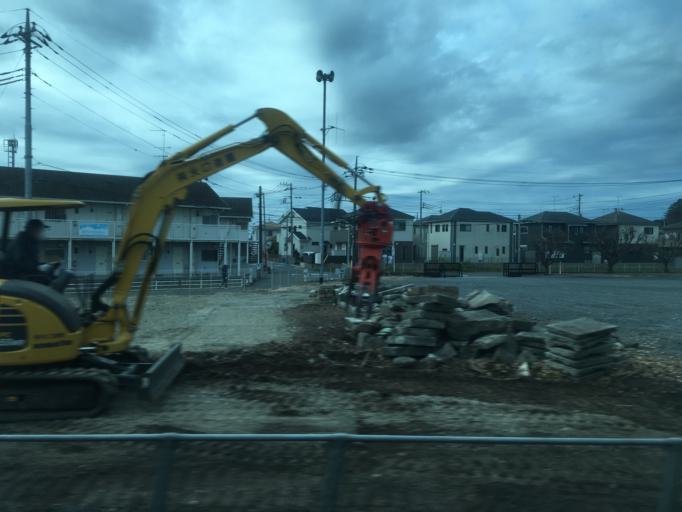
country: JP
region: Saitama
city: Okegawa
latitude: 36.0265
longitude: 139.5375
